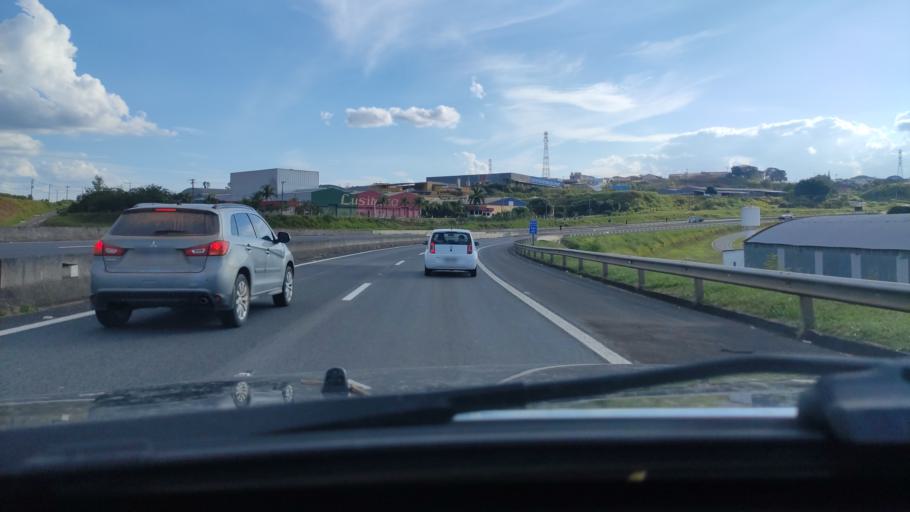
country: BR
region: Sao Paulo
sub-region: Itapira
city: Itapira
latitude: -22.4512
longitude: -46.8402
